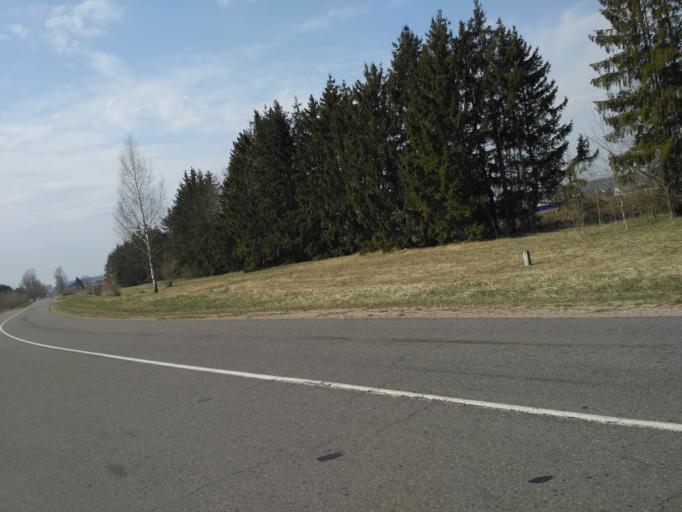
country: BY
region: Minsk
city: Zamostochcha
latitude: 53.8940
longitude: 27.9273
